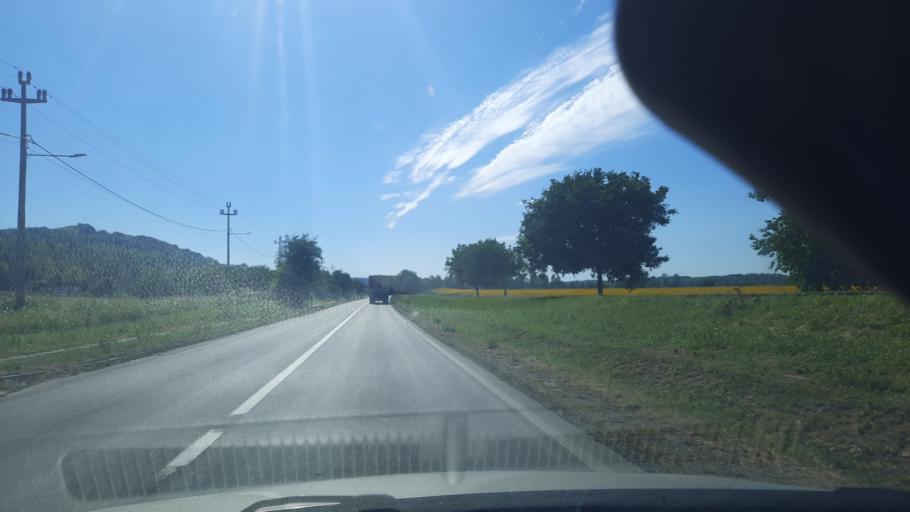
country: RS
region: Autonomna Pokrajina Vojvodina
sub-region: Juznobacki Okrug
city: Beocin
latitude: 45.2087
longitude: 19.7435
